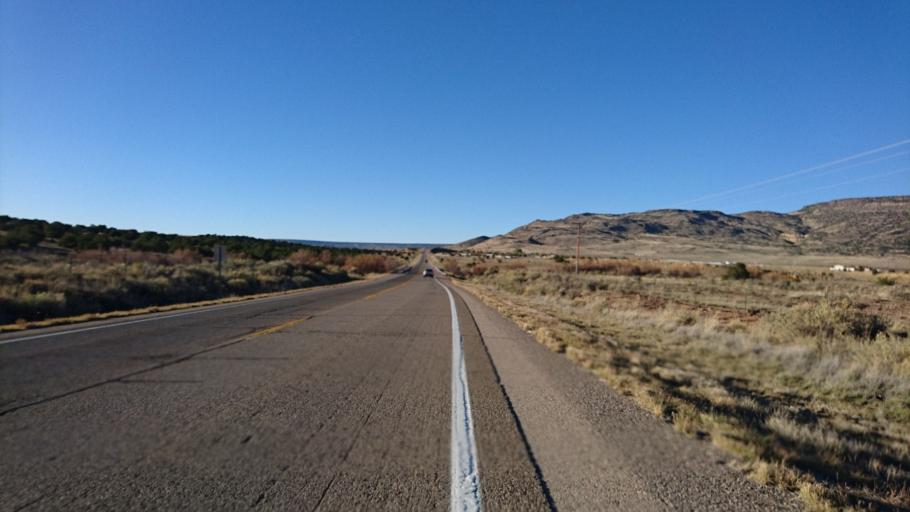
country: US
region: New Mexico
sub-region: Cibola County
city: Grants
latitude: 35.0962
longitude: -107.7725
